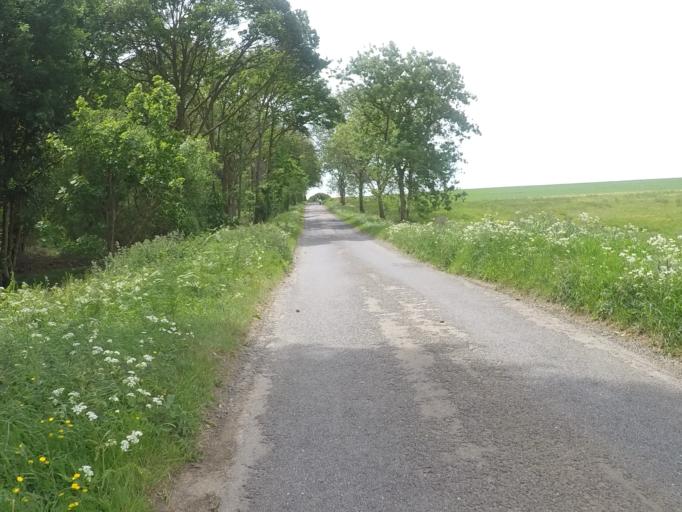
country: GB
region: England
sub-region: Oxfordshire
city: Charlbury
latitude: 51.8524
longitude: -1.5289
